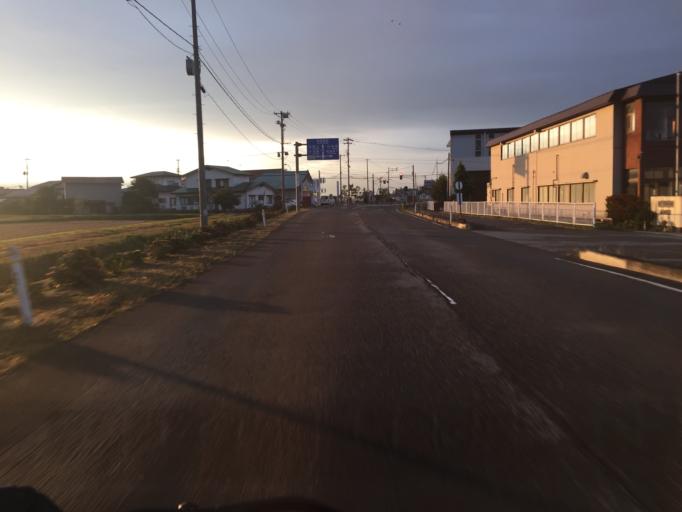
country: JP
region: Fukushima
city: Kitakata
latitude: 37.5553
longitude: 139.8915
